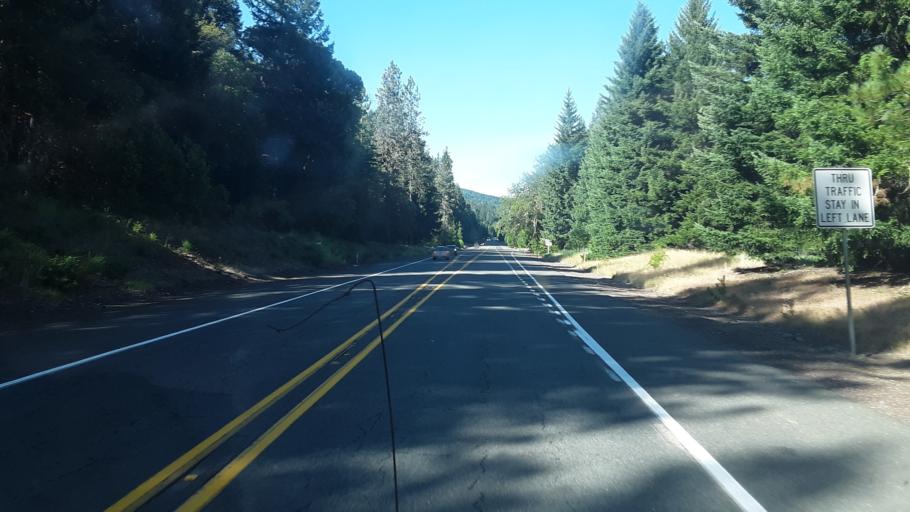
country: US
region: Oregon
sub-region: Jackson County
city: Shady Cove
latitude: 42.6846
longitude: -122.6113
